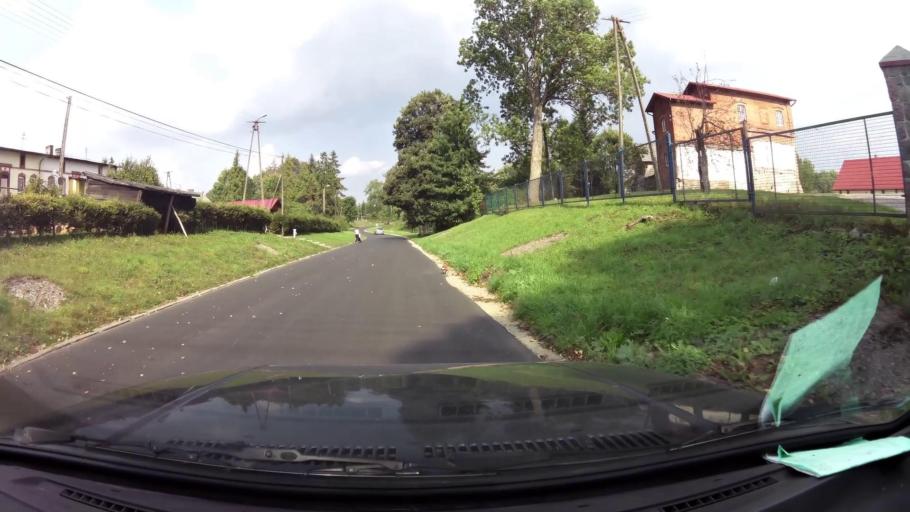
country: PL
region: Pomeranian Voivodeship
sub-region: Powiat slupski
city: Kepice
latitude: 54.1667
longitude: 16.8209
